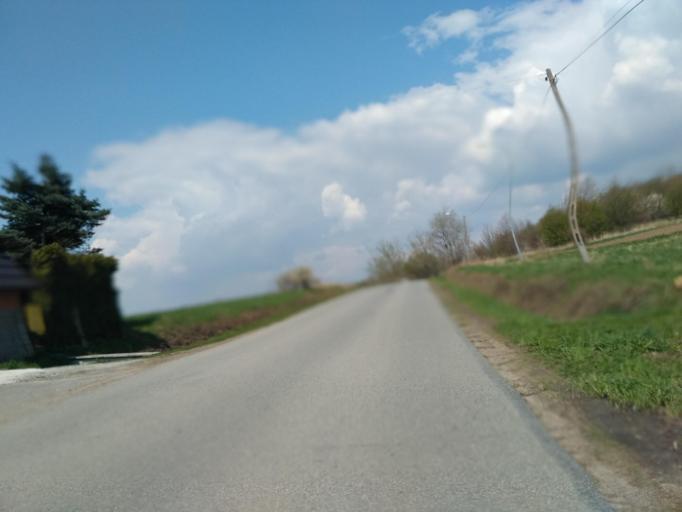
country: PL
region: Subcarpathian Voivodeship
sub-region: Powiat sanocki
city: Nowosielce-Gniewosz
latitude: 49.5391
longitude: 22.1148
